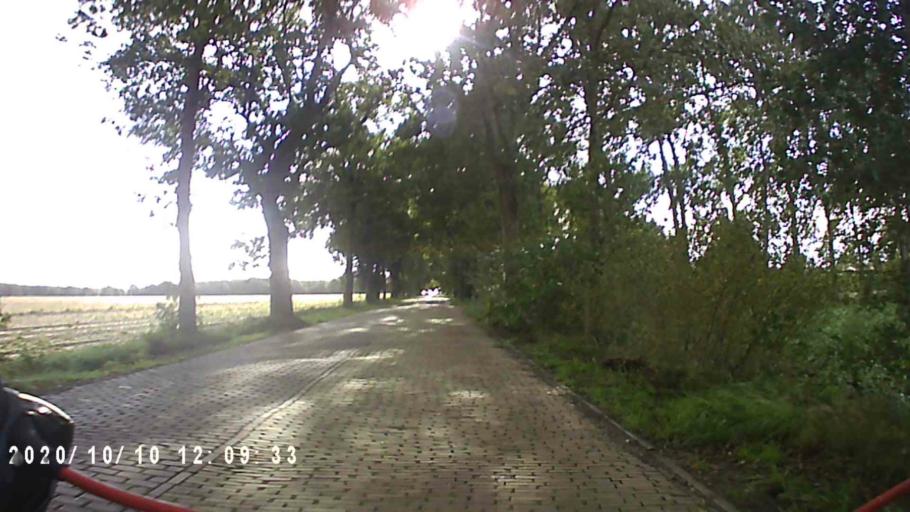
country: NL
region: Friesland
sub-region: Gemeente Heerenveen
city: Jubbega
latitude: 53.0456
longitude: 6.1448
